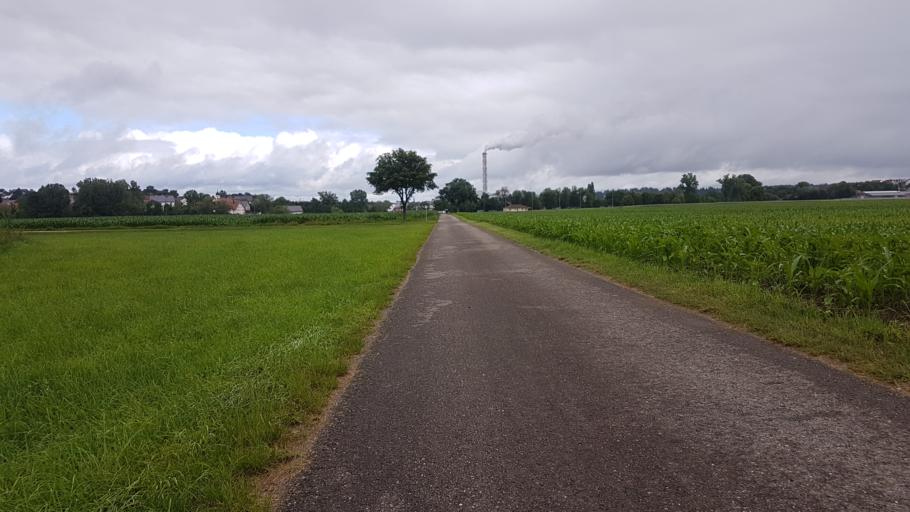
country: DE
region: Baden-Wuerttemberg
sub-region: Tuebingen Region
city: Dettingen
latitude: 48.2558
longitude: 9.7243
